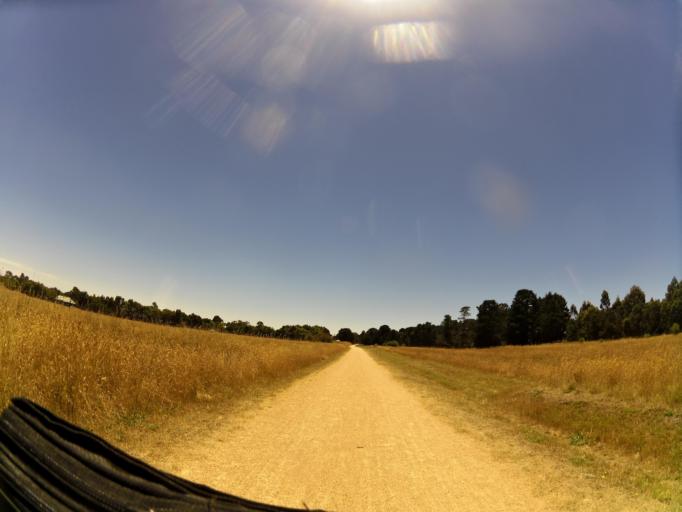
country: AU
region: Victoria
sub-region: Ballarat North
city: Delacombe
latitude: -37.5922
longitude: 143.7213
